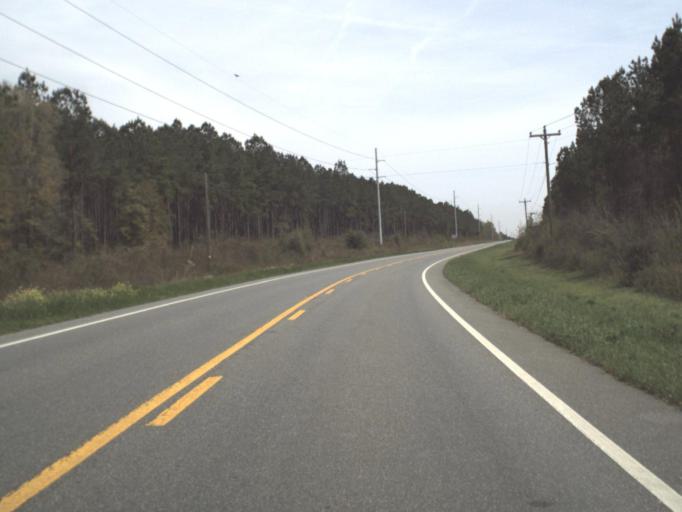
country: US
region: Alabama
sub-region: Houston County
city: Cottonwood
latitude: 30.9485
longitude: -85.3620
